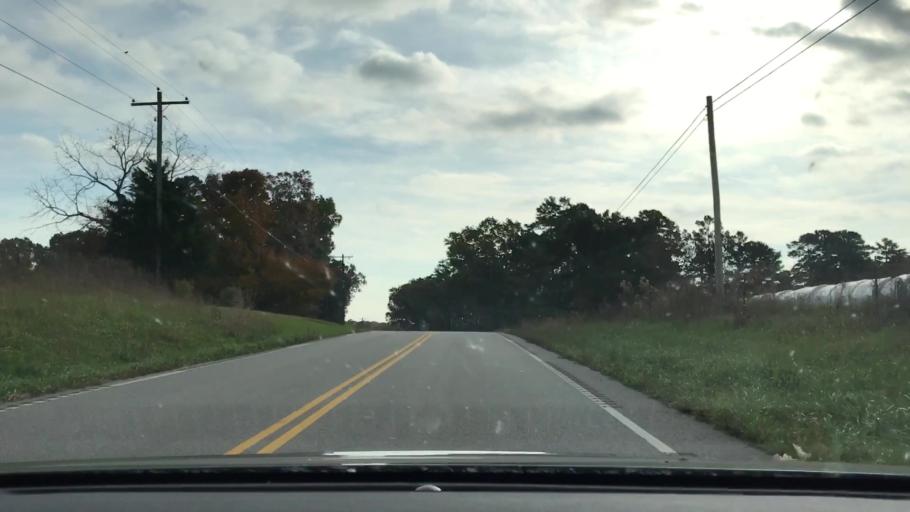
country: US
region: Tennessee
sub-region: Fentress County
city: Jamestown
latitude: 36.3847
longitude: -84.9262
